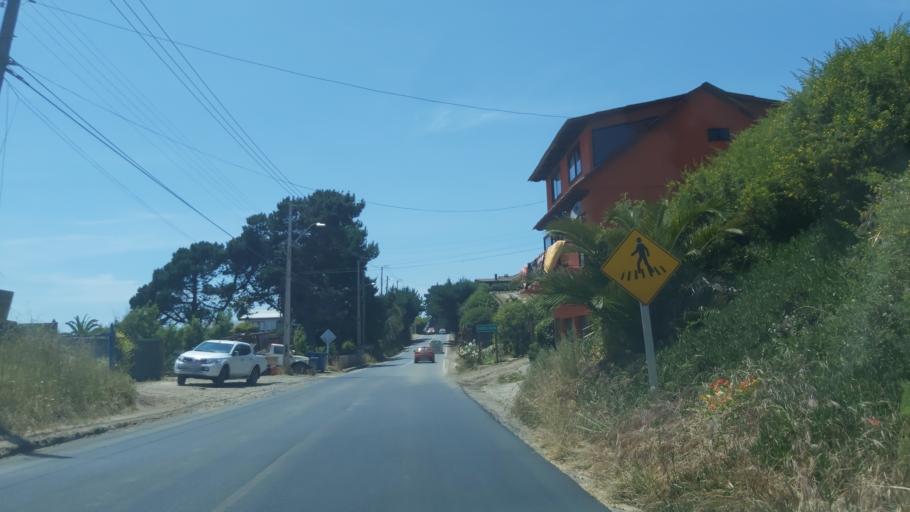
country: CL
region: Maule
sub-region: Provincia de Cauquenes
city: Cauquenes
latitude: -35.8185
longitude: -72.5941
